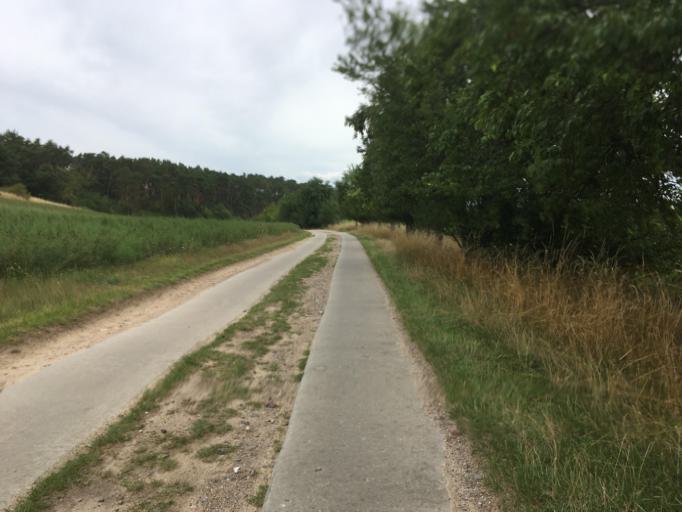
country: DE
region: Brandenburg
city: Gerswalde
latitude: 53.1889
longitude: 13.8336
